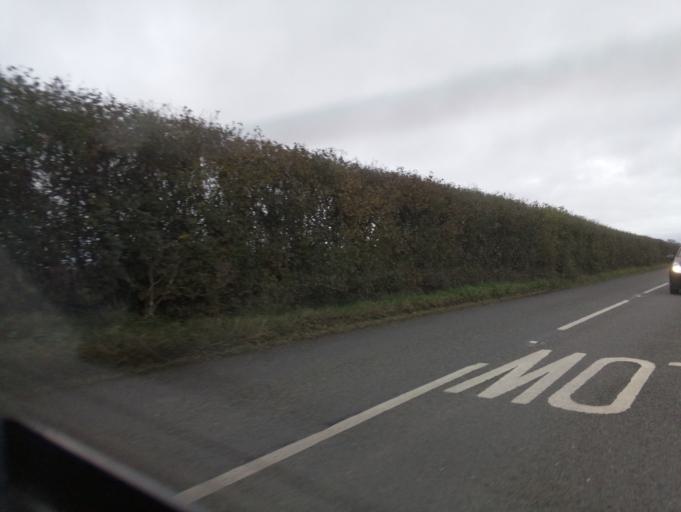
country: GB
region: England
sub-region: Dorset
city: Sherborne
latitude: 50.9757
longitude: -2.5598
